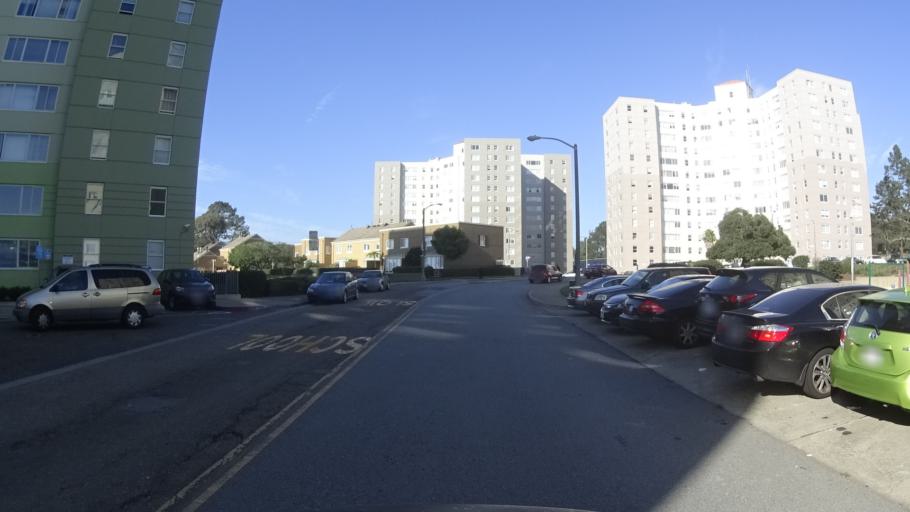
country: US
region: California
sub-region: San Mateo County
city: Daly City
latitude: 37.7143
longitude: -122.4734
